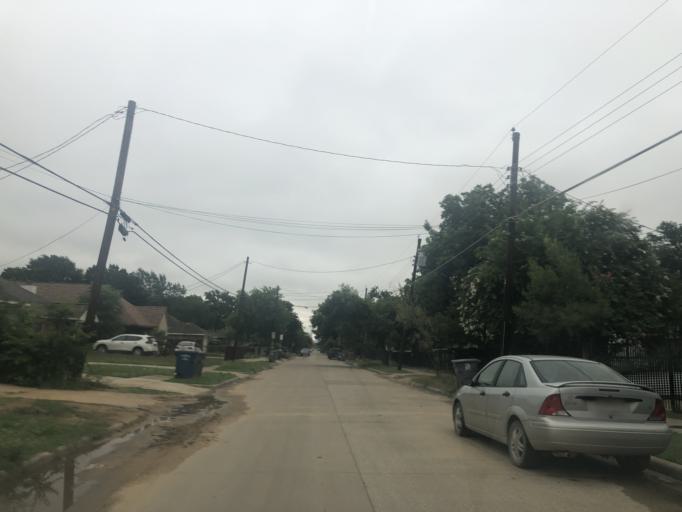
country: US
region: Texas
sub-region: Dallas County
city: Cockrell Hill
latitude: 32.7838
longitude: -96.8806
